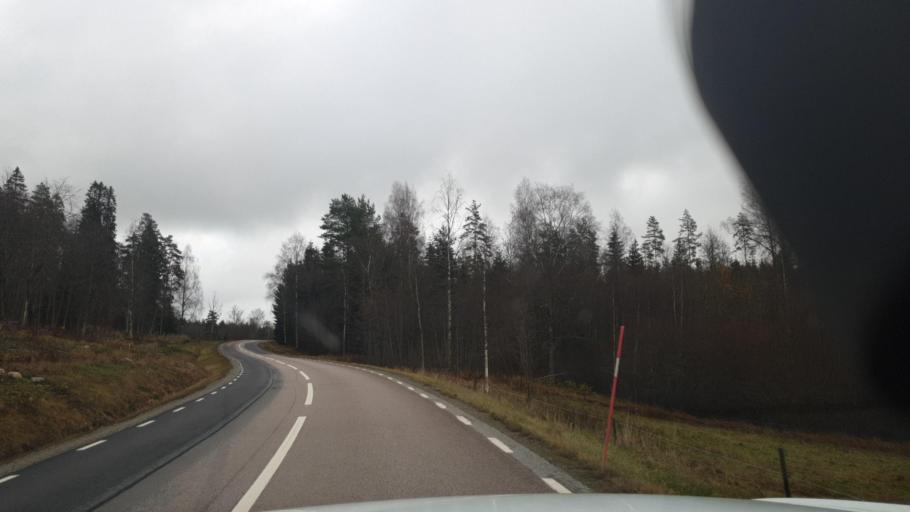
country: SE
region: Vaermland
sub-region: Sunne Kommun
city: Sunne
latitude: 59.6679
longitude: 12.9839
